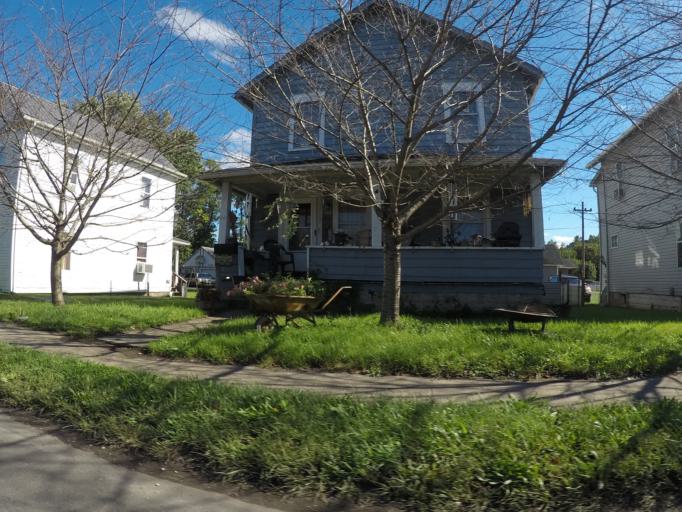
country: US
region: Ohio
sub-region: Lawrence County
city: Burlington
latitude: 38.4073
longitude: -82.4968
